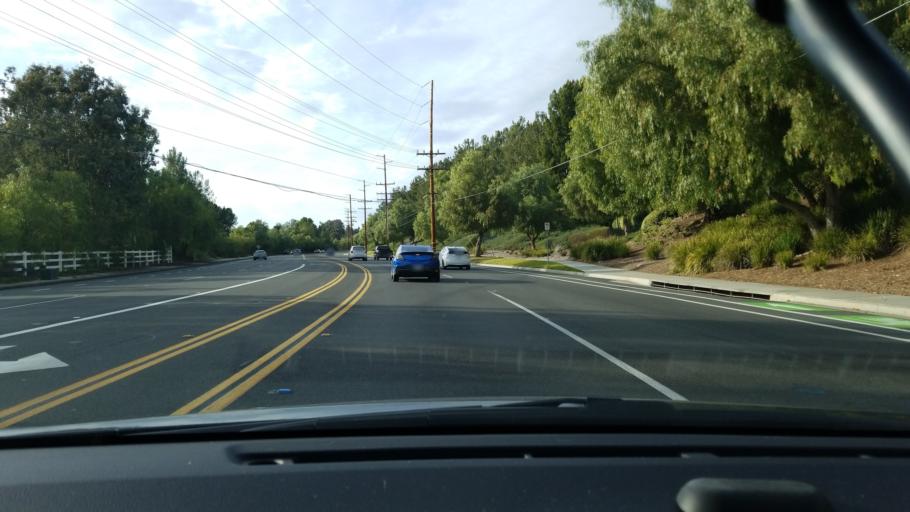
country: US
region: California
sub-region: Riverside County
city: Temecula
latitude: 33.4876
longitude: -117.1054
